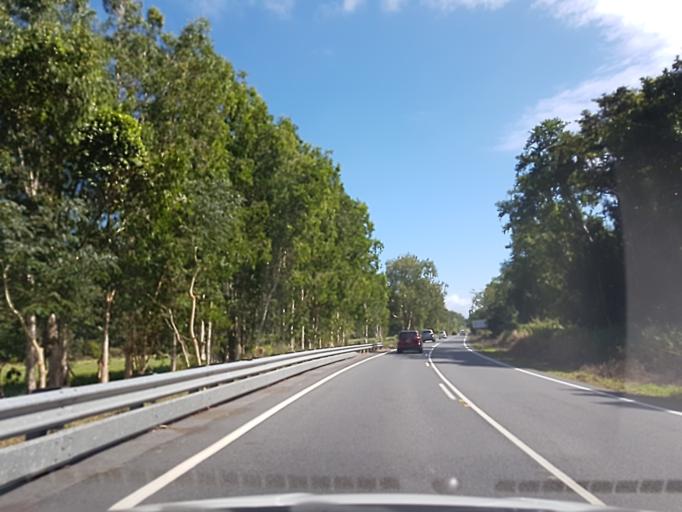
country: AU
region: Queensland
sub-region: Cairns
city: Port Douglas
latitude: -16.5708
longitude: 145.5073
